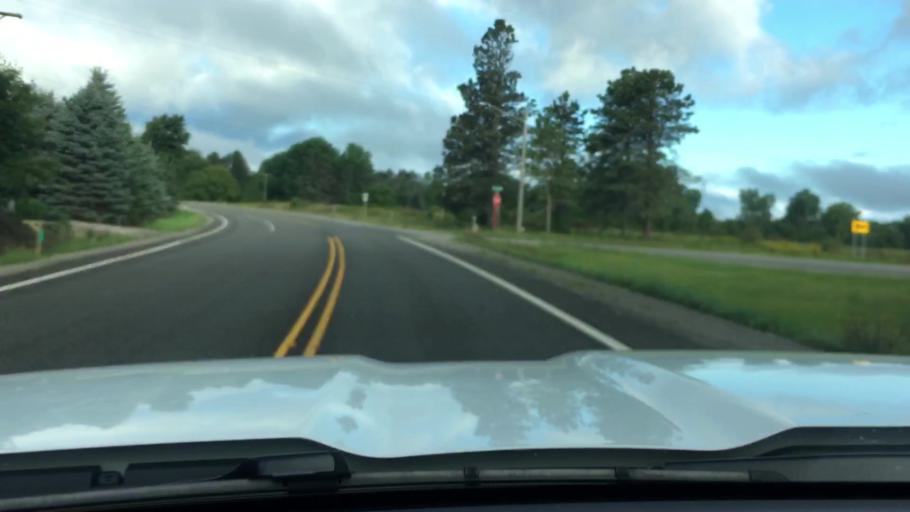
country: US
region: Michigan
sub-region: Lapeer County
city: Barnes Lake-Millers Lake
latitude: 43.3367
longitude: -83.3261
